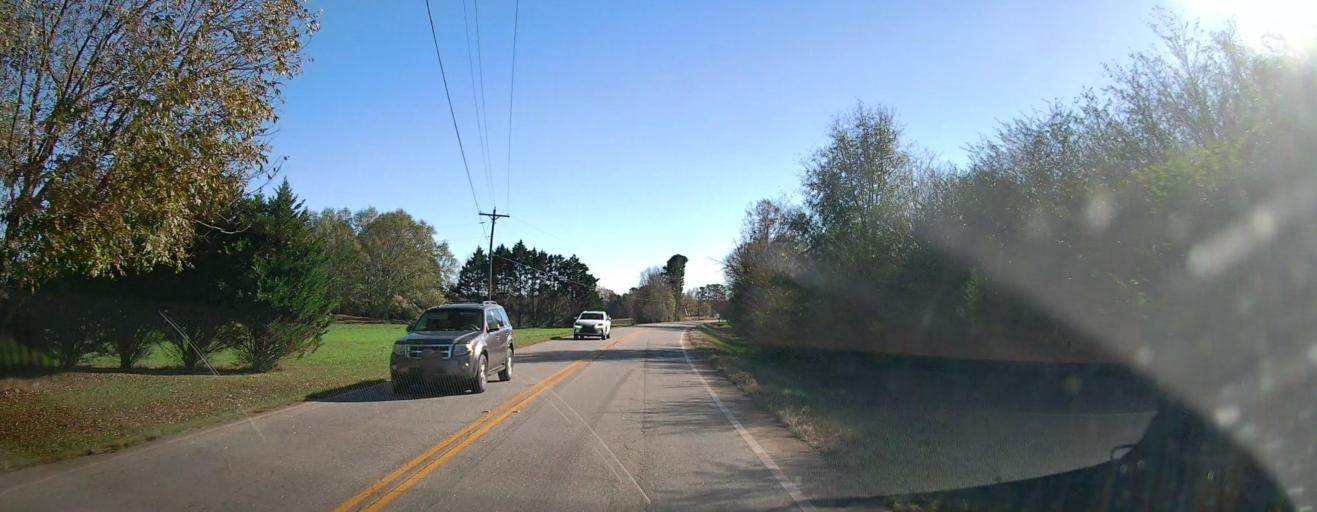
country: US
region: Georgia
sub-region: Hall County
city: Lula
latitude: 34.4520
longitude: -83.7282
